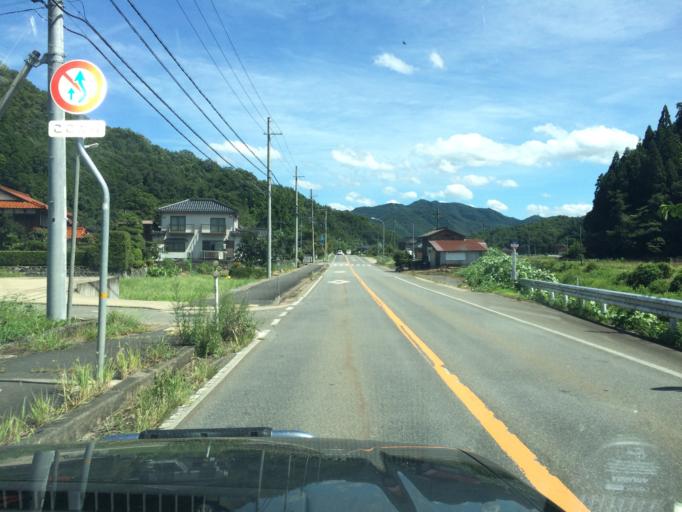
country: JP
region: Hyogo
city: Toyooka
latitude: 35.4656
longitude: 134.8386
